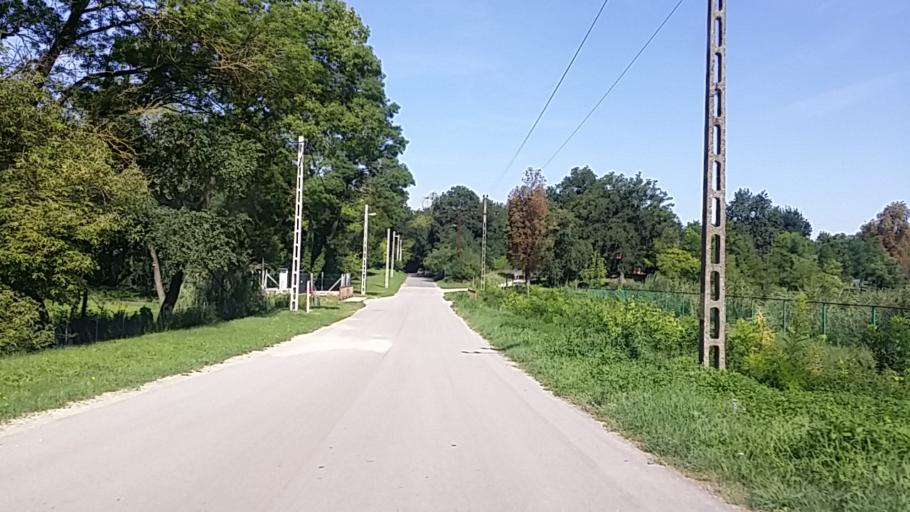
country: HU
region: Fejer
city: Deg
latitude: 46.8748
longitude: 18.4396
